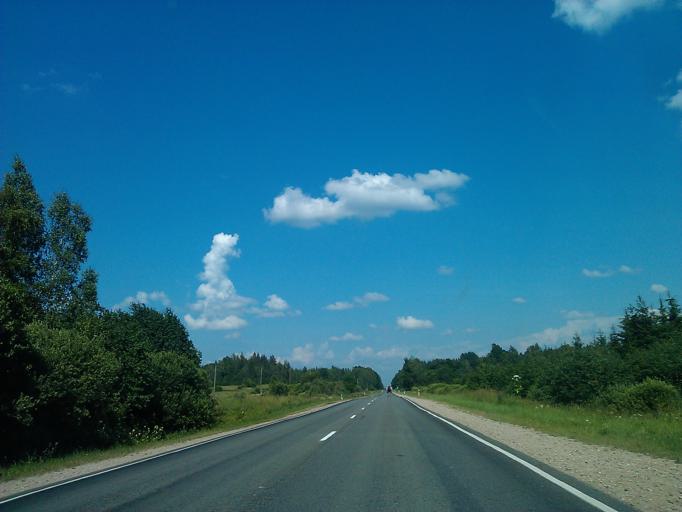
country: LV
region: Skrunda
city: Skrunda
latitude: 56.6496
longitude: 21.9090
